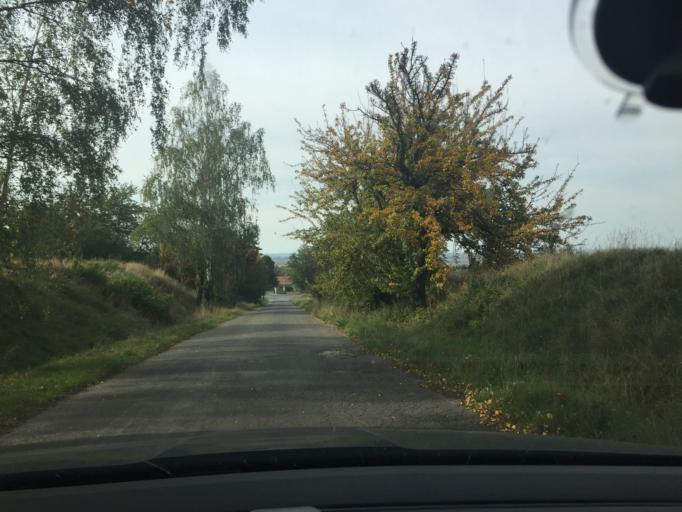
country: CZ
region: Central Bohemia
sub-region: Okres Kutna Hora
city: Kutna Hora
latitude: 49.9770
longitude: 15.2756
